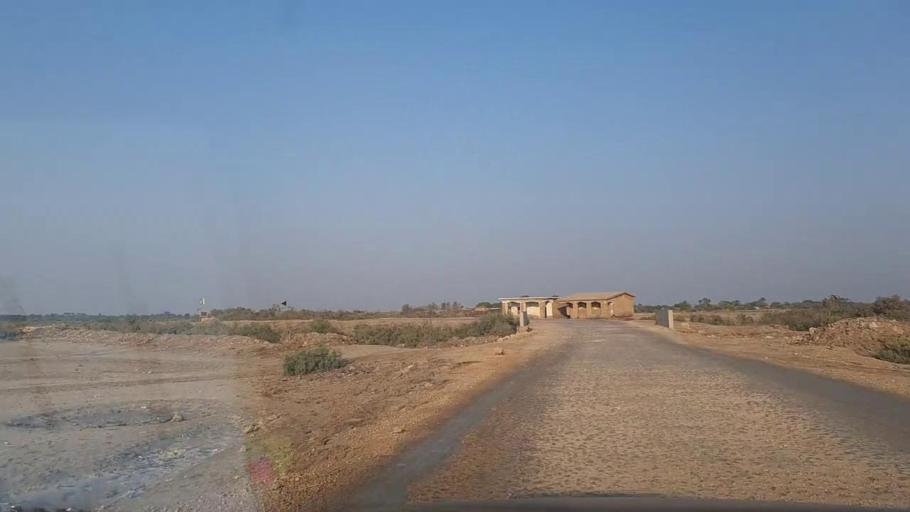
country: PK
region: Sindh
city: Keti Bandar
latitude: 24.2750
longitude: 67.5863
